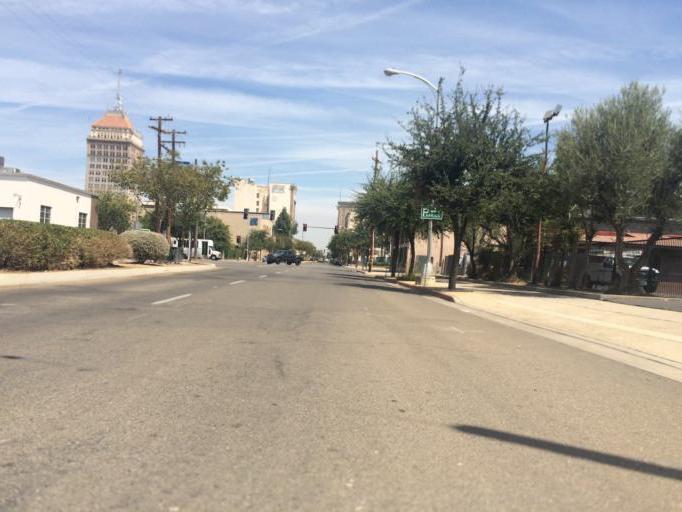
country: US
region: California
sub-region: Fresno County
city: Fresno
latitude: 36.7319
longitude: -119.7929
